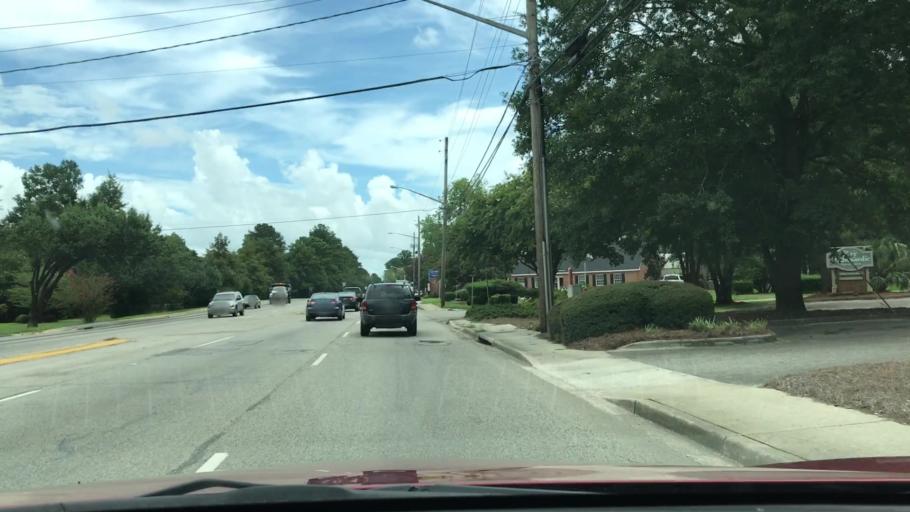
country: US
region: South Carolina
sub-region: Georgetown County
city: Georgetown
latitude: 33.3855
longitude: -79.2883
